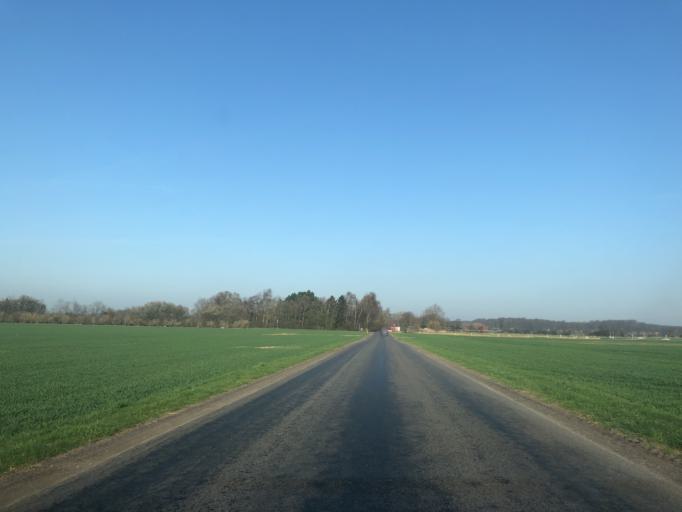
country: DK
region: Zealand
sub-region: Stevns Kommune
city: Store Heddinge
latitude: 55.2804
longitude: 12.3174
